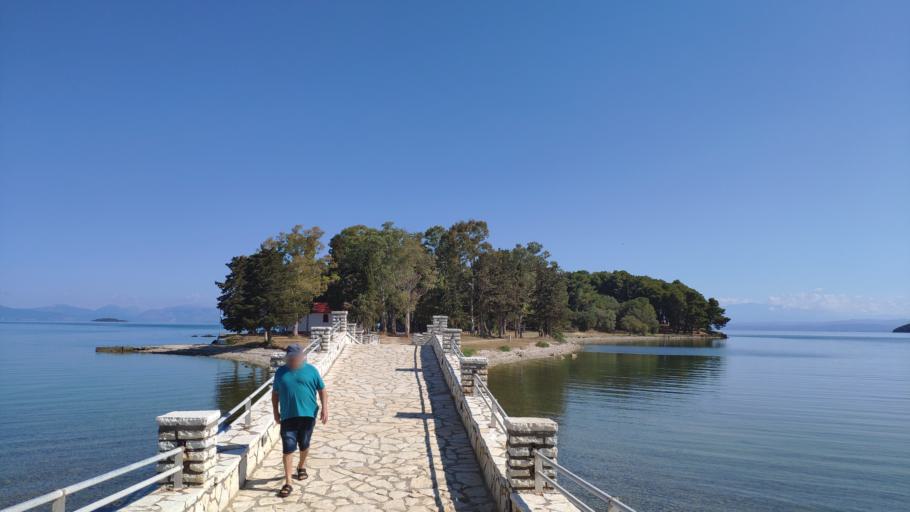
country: GR
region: West Greece
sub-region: Nomos Aitolias kai Akarnanias
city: Vonitsa
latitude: 38.9237
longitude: 20.9002
